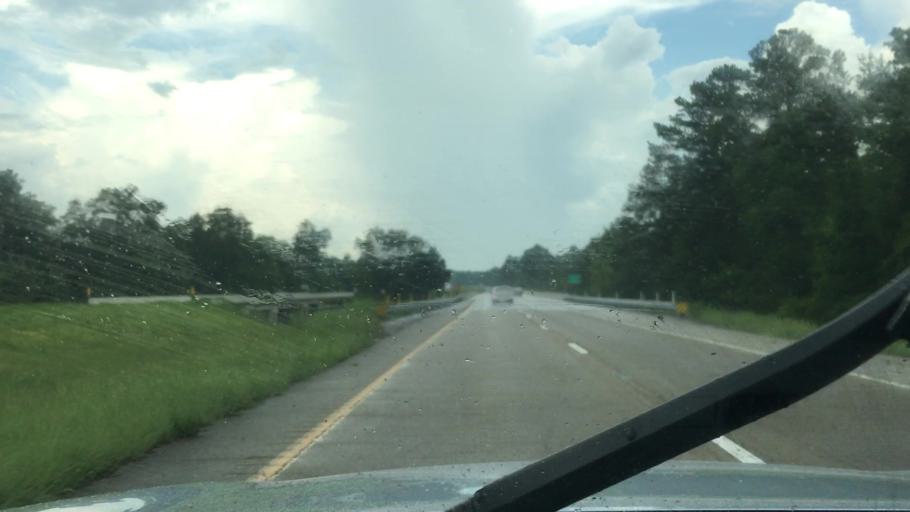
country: US
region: Mississippi
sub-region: Lamar County
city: Purvis
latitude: 31.1675
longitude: -89.3527
